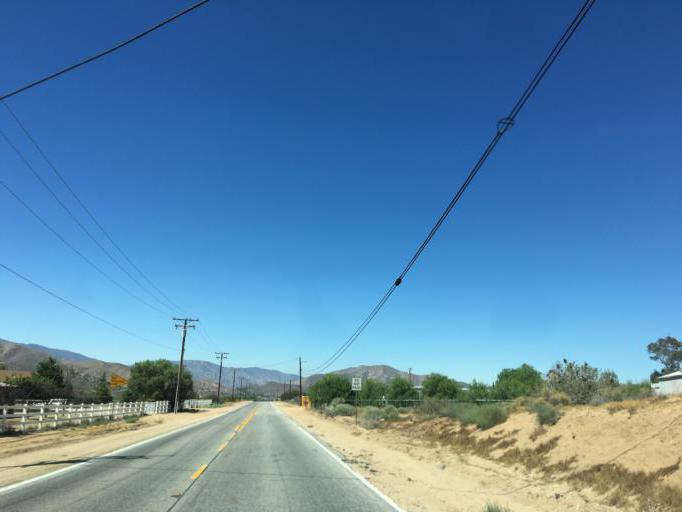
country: US
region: California
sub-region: Los Angeles County
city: Vincent
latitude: 34.4854
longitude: -118.1411
